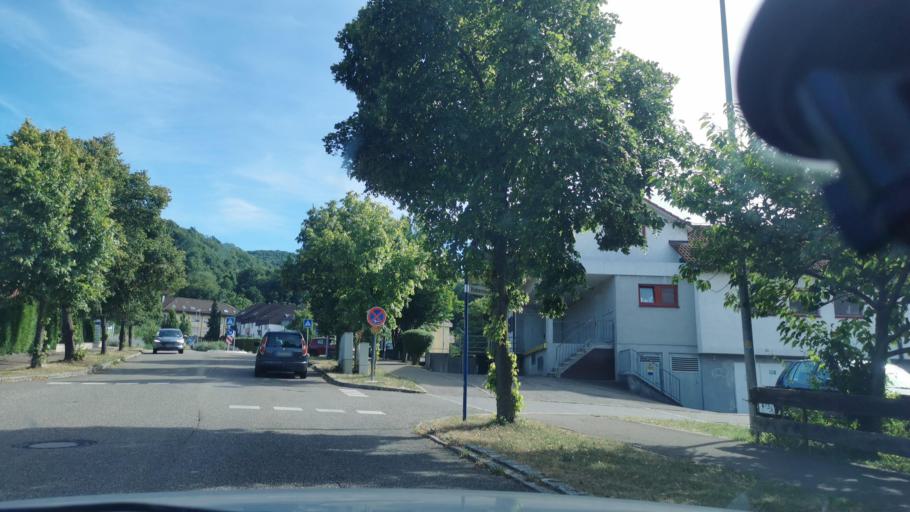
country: DE
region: Baden-Wuerttemberg
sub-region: Regierungsbezirk Stuttgart
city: Heubach
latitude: 48.7955
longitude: 9.9222
